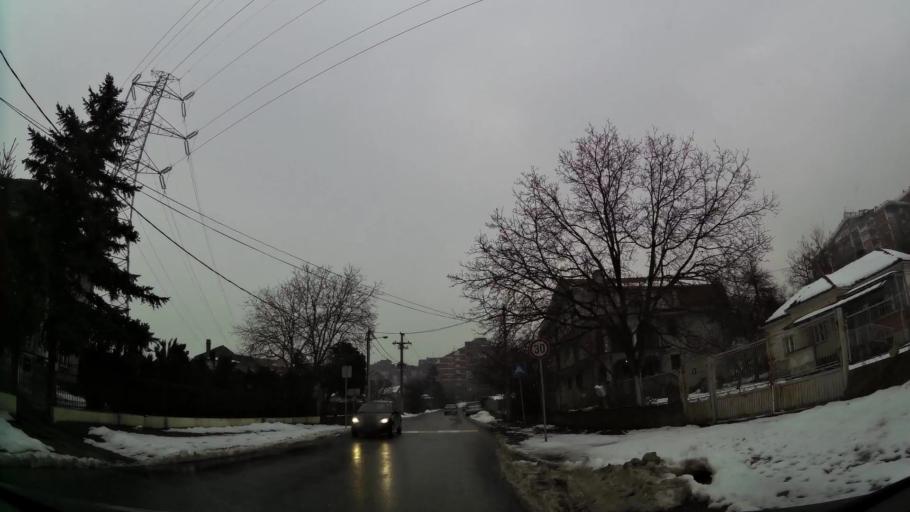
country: RS
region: Central Serbia
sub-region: Belgrade
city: Zvezdara
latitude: 44.7742
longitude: 20.5115
